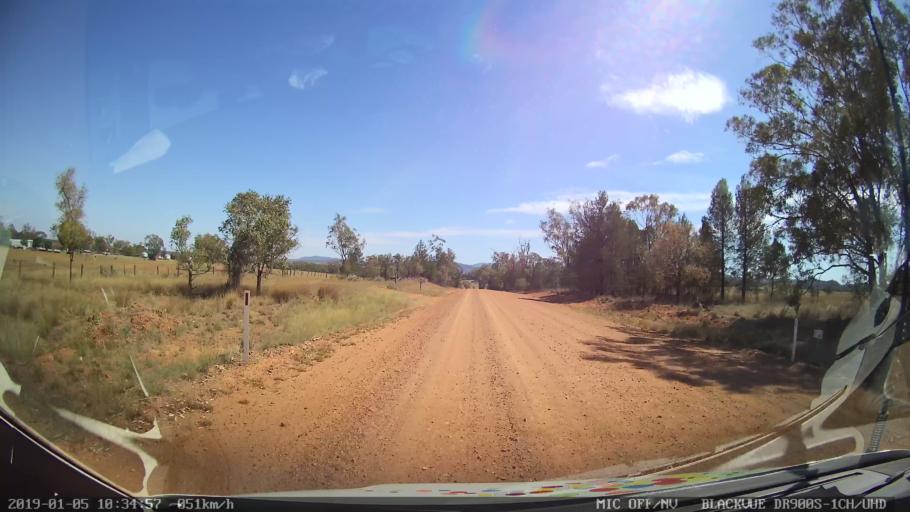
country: AU
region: New South Wales
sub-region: Gilgandra
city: Gilgandra
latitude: -31.4942
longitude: 148.9294
